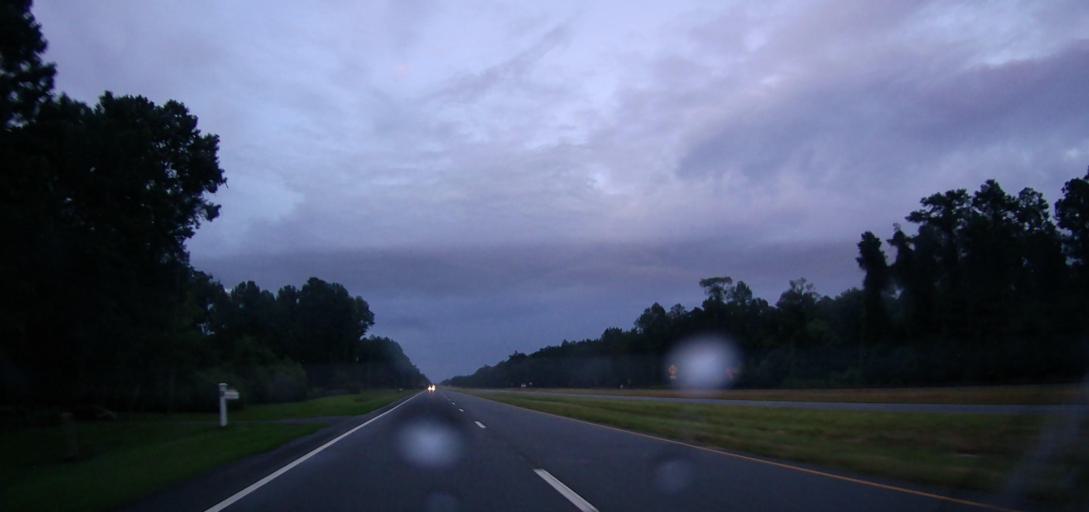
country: US
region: Georgia
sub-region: Lowndes County
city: Valdosta
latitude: 30.8852
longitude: -83.1379
